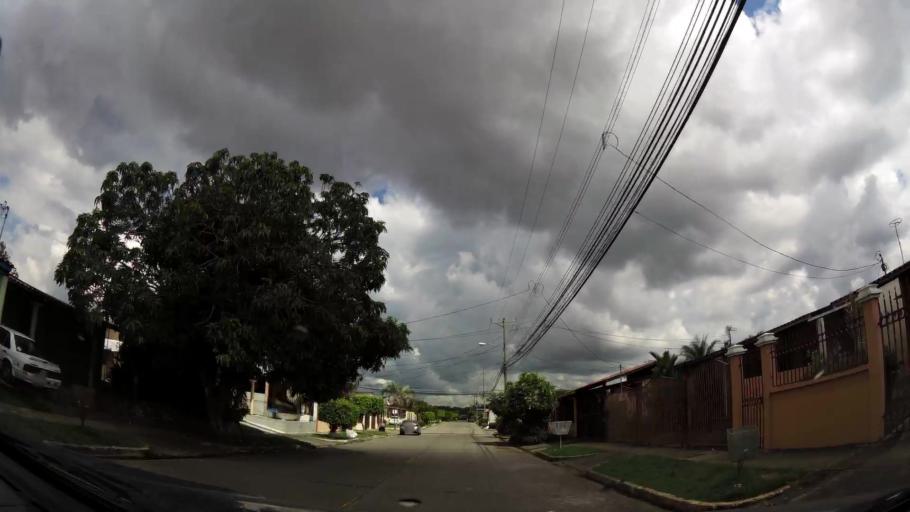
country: PA
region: Panama
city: Nuevo Arraijan
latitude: 8.9291
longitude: -79.7262
